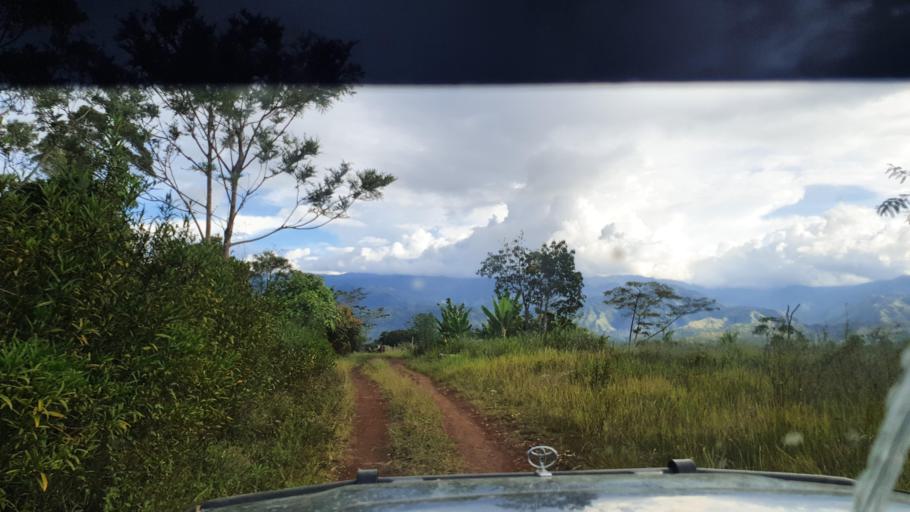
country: PG
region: Jiwaka
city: Minj
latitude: -5.9163
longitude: 144.8201
